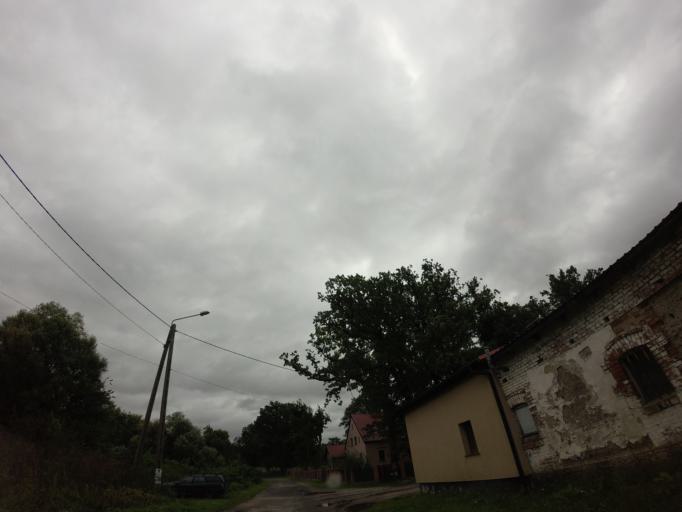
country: PL
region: West Pomeranian Voivodeship
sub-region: Powiat choszczenski
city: Choszczno
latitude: 53.1625
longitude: 15.3734
